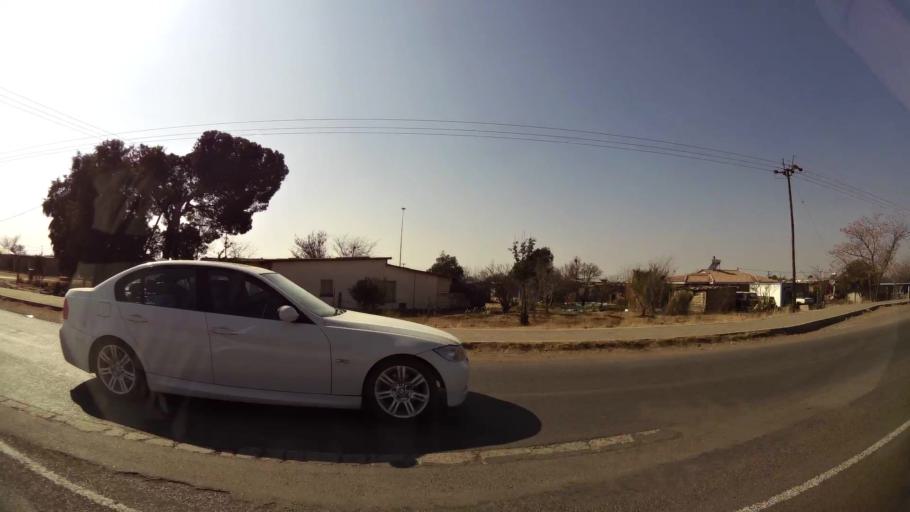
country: ZA
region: Orange Free State
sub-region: Mangaung Metropolitan Municipality
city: Bloemfontein
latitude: -29.1805
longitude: 26.2668
